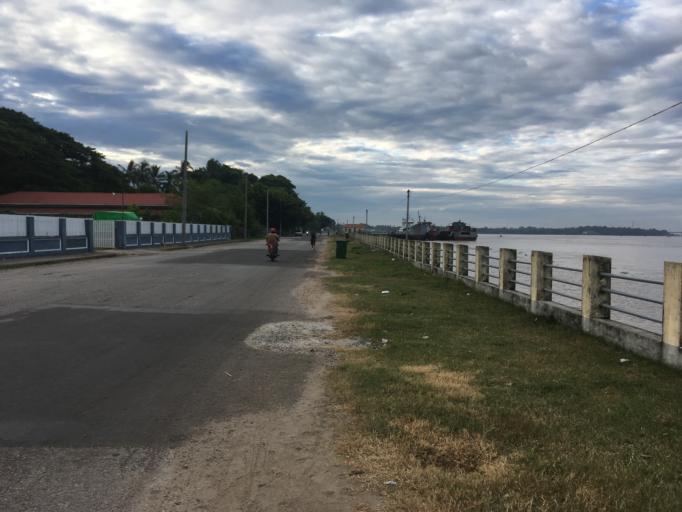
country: MM
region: Mon
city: Mawlamyine
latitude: 16.4679
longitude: 97.6217
